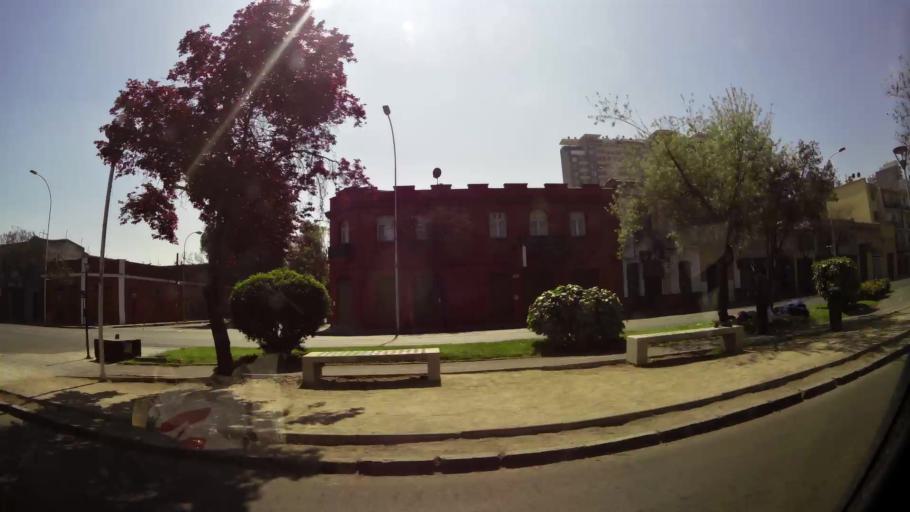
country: CL
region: Santiago Metropolitan
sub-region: Provincia de Santiago
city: Santiago
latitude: -33.4564
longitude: -70.6340
